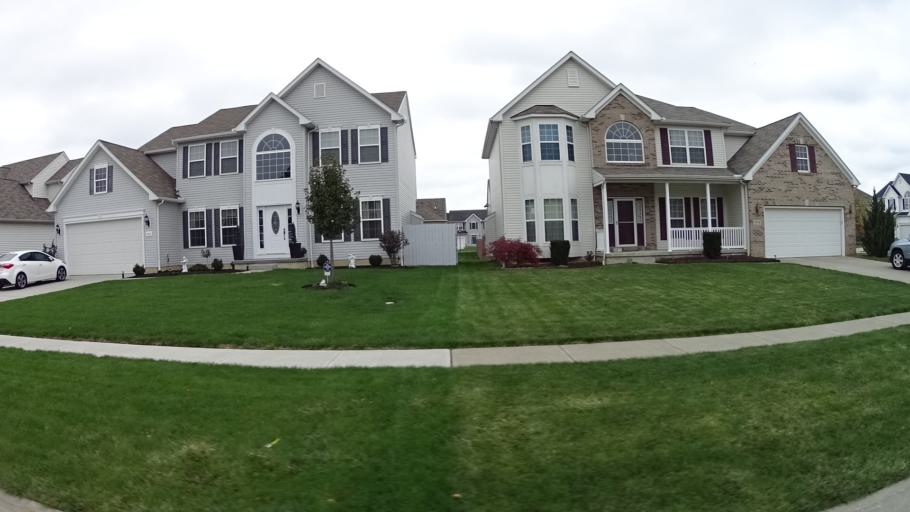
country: US
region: Ohio
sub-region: Lorain County
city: Amherst
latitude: 41.4300
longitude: -82.2185
